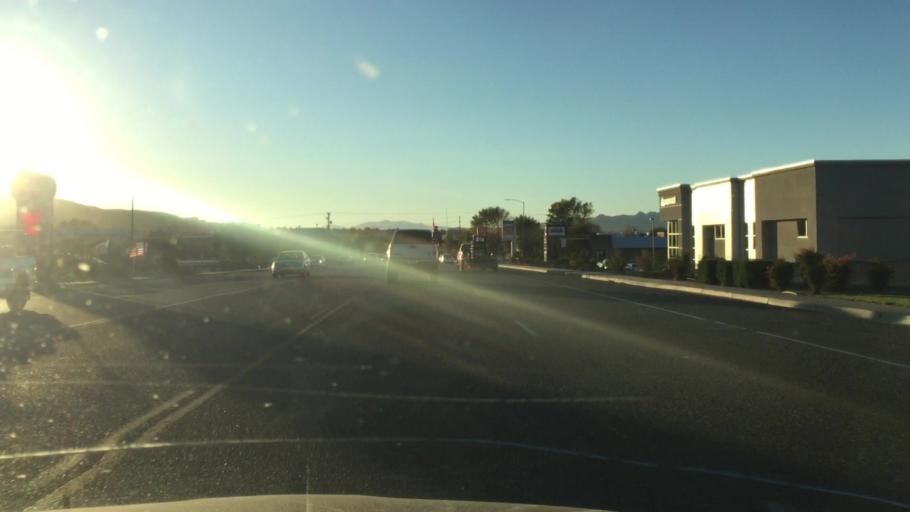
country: US
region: Utah
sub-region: Washington County
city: Hurricane
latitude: 37.1761
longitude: -113.3059
